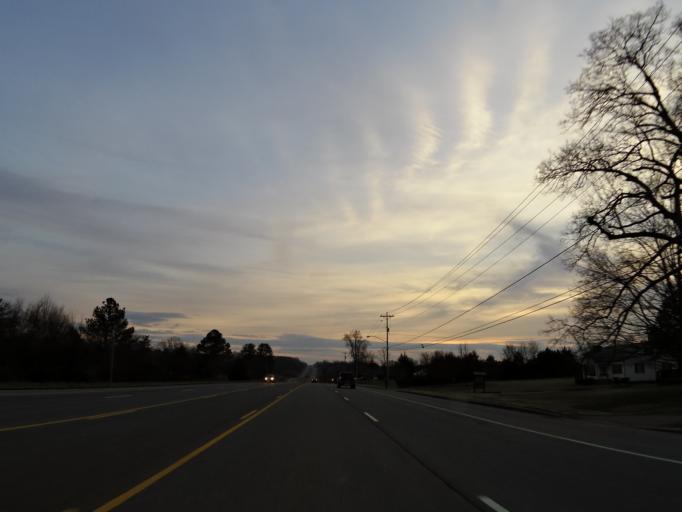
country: US
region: Tennessee
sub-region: McMinn County
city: Englewood
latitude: 35.4154
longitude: -84.4931
